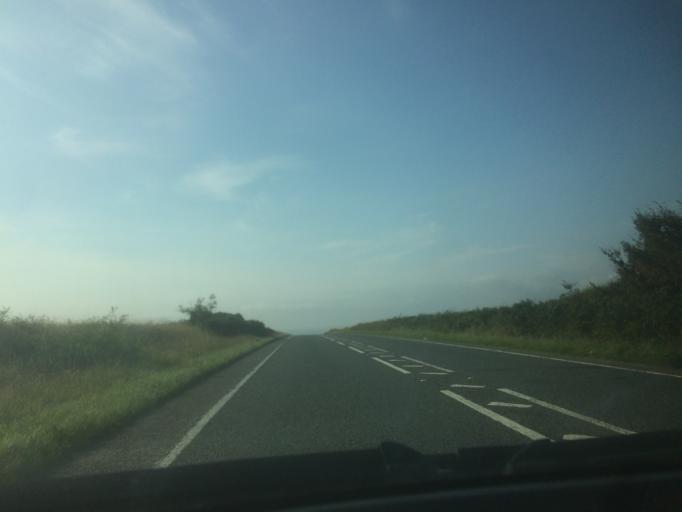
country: GB
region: England
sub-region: Cornwall
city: Callington
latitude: 50.4829
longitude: -4.2863
